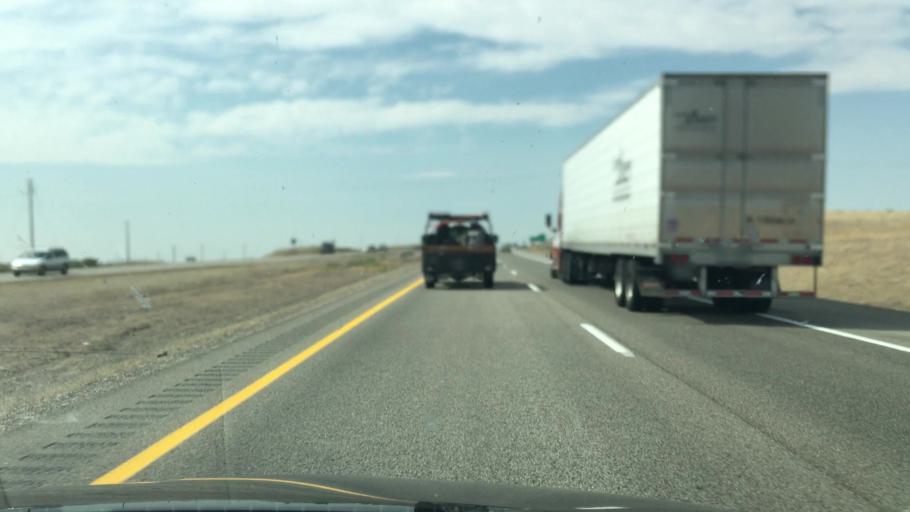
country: US
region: Idaho
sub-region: Ada County
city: Boise
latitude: 43.4606
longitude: -116.0891
